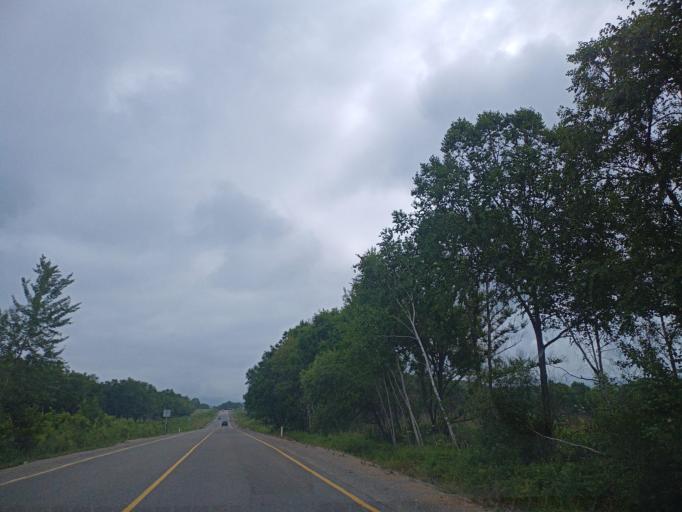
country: RU
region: Primorskiy
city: Dal'nerechensk
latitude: 46.0389
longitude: 133.8898
